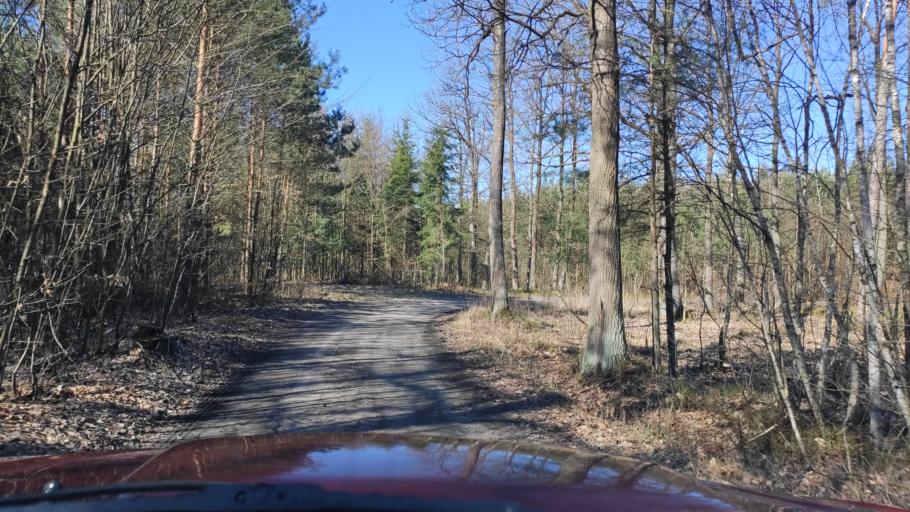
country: PL
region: Masovian Voivodeship
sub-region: Powiat kozienicki
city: Garbatka-Letnisko
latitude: 51.4418
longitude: 21.5366
